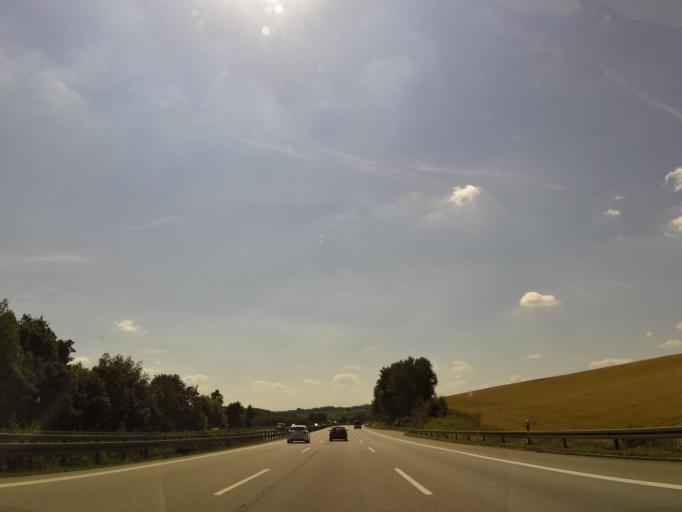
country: DE
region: Bavaria
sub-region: Upper Bavaria
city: Rohrbach
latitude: 48.6007
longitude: 11.5556
